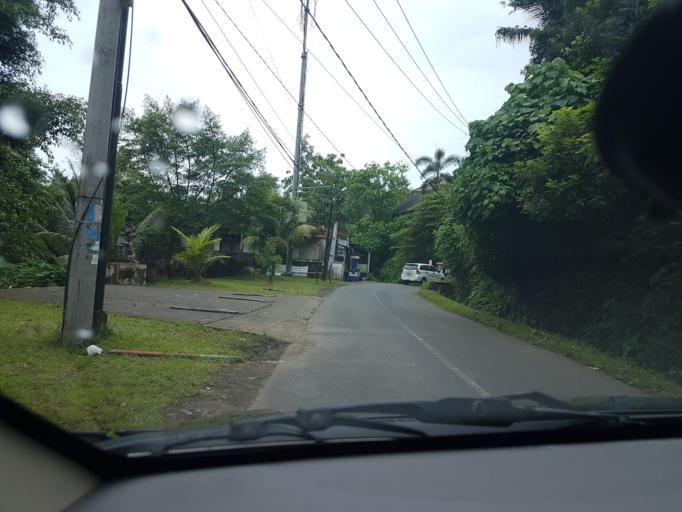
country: ID
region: Bali
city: Banjar Pande
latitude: -8.5038
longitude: 115.2459
